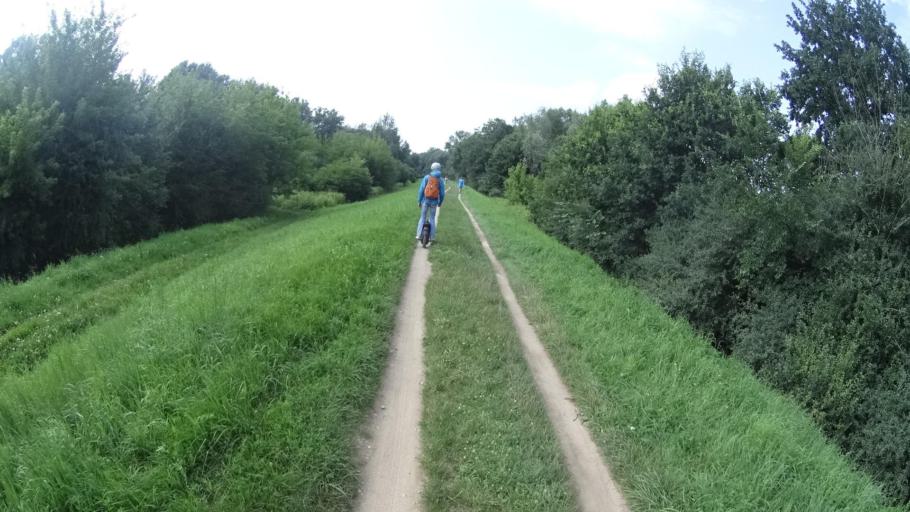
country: PL
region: Masovian Voivodeship
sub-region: Powiat legionowski
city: Jablonna
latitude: 52.3679
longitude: 20.9167
